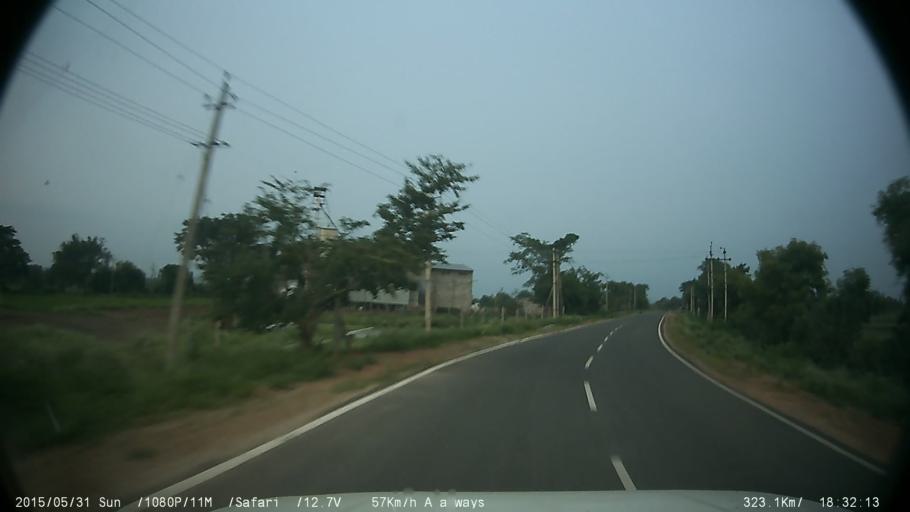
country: IN
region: Karnataka
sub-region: Mysore
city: Nanjangud
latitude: 12.1326
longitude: 76.7461
